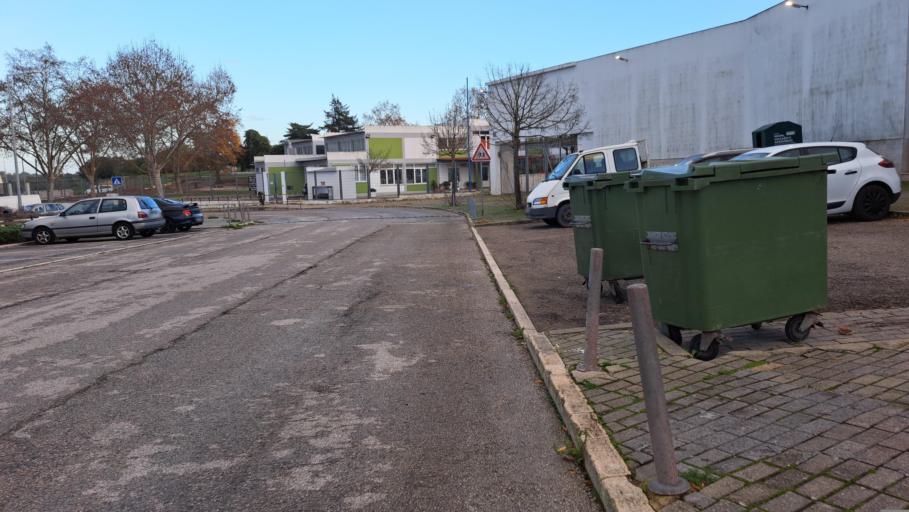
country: PT
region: Setubal
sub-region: Moita
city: Alhos Vedros
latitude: 38.6437
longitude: -9.0366
